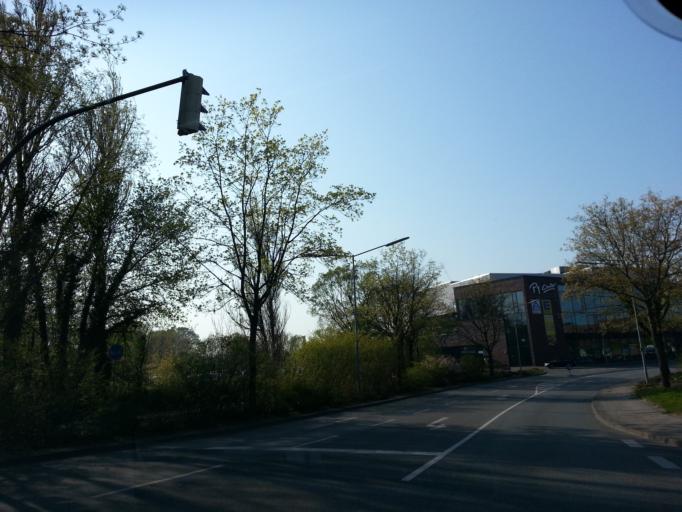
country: DE
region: Schleswig-Holstein
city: Bad Schwartau
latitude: 53.9176
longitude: 10.6959
